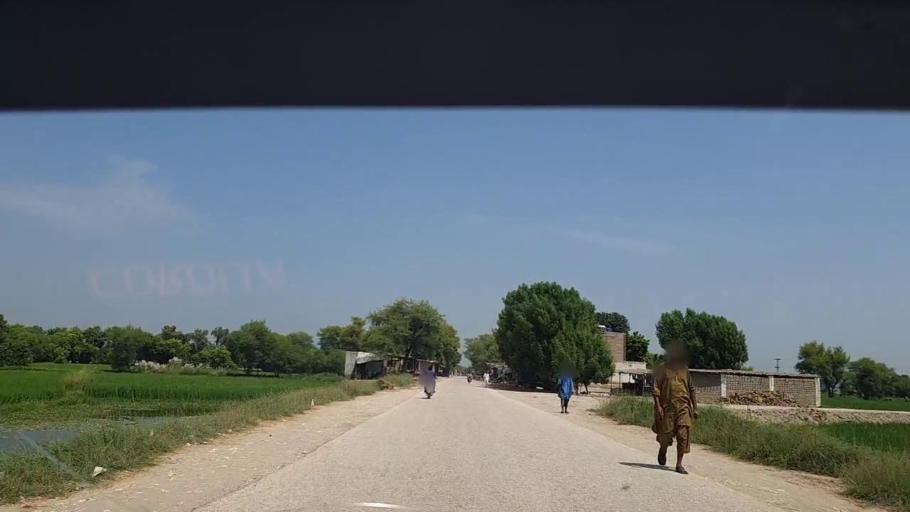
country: PK
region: Sindh
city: Rustam jo Goth
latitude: 28.0827
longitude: 68.7869
